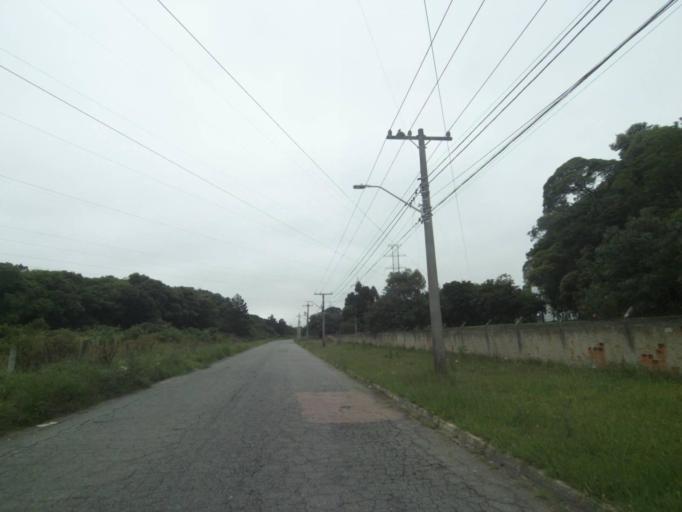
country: BR
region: Parana
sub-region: Araucaria
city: Araucaria
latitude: -25.5421
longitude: -49.3202
